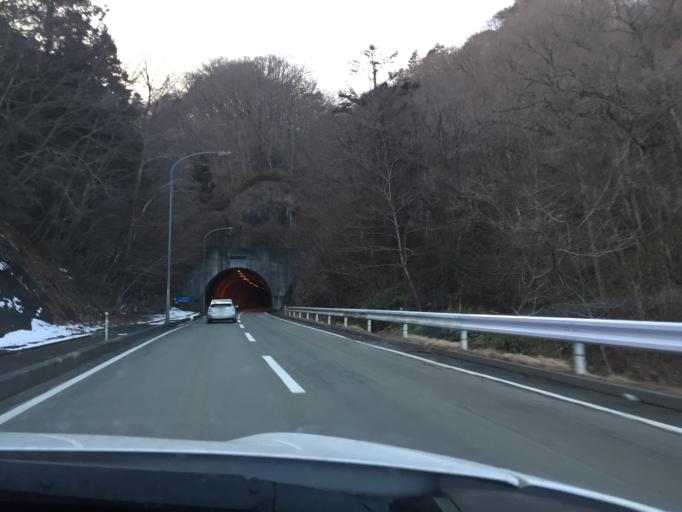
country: JP
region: Fukushima
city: Namie
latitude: 37.5257
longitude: 140.8805
